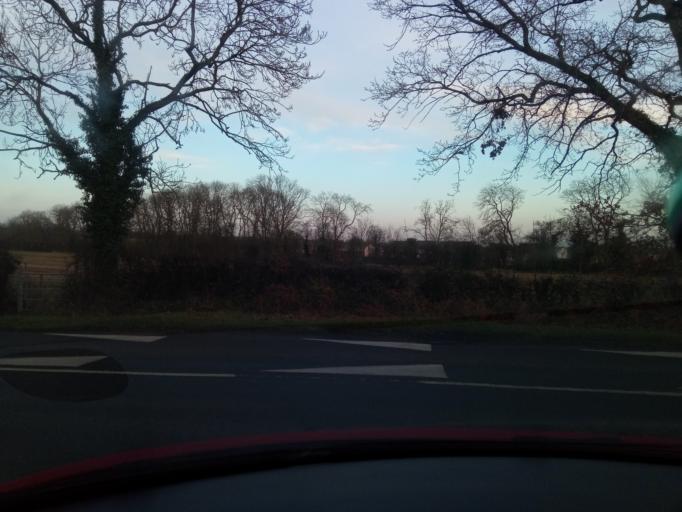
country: GB
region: England
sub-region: Leicestershire
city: Mountsorrel
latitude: 52.7237
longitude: -1.1571
